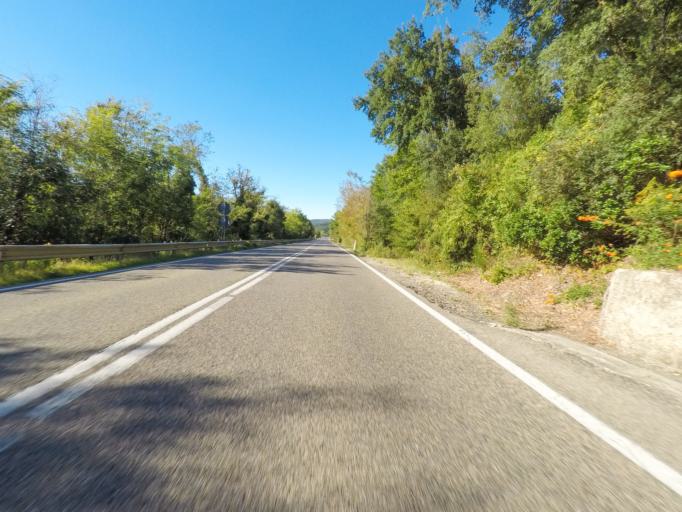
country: IT
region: Tuscany
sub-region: Provincia di Grosseto
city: Civitella Marittima
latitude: 43.0183
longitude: 11.2848
